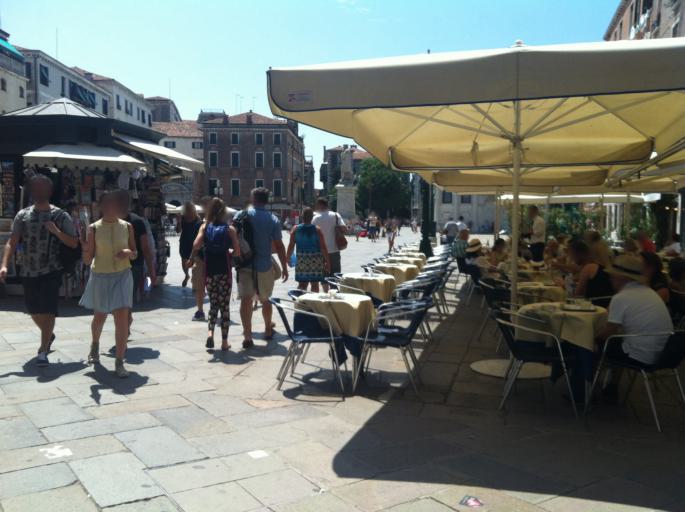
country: IT
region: Veneto
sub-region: Provincia di Venezia
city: Venice
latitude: 45.4337
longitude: 12.3307
